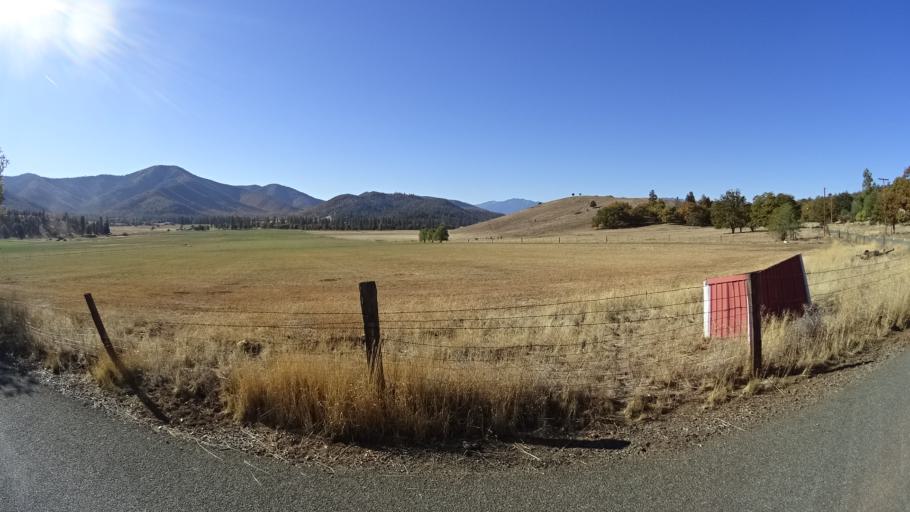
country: US
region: California
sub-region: Siskiyou County
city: Yreka
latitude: 41.5814
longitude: -122.7942
